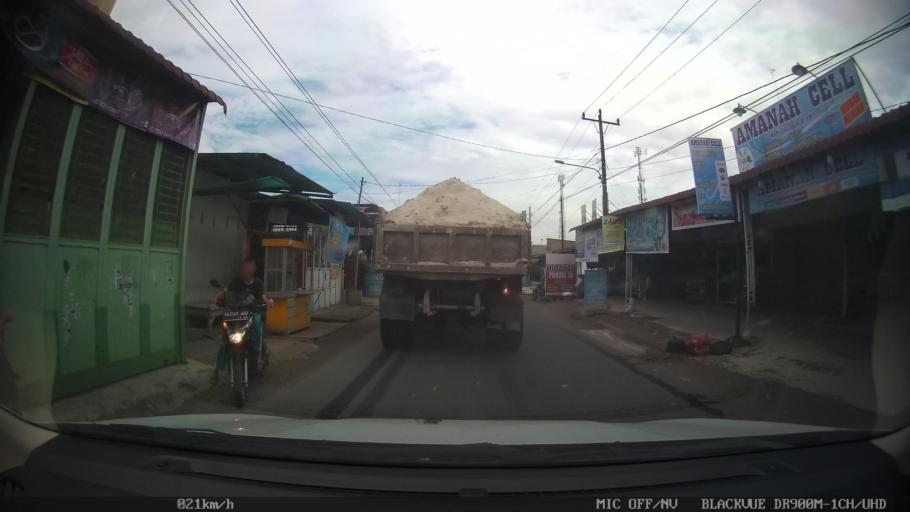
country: ID
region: North Sumatra
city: Sunggal
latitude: 3.6296
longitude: 98.5940
